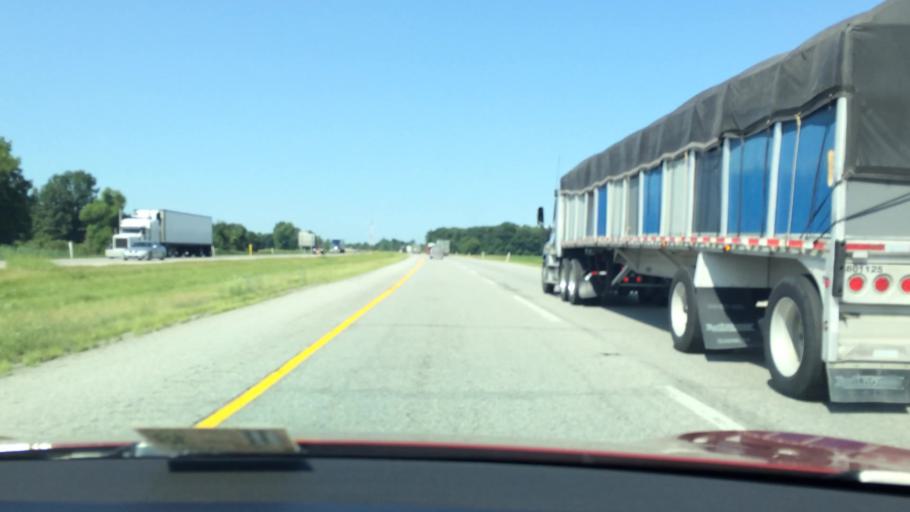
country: US
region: Indiana
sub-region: Elkhart County
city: Middlebury
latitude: 41.7465
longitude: -85.7103
